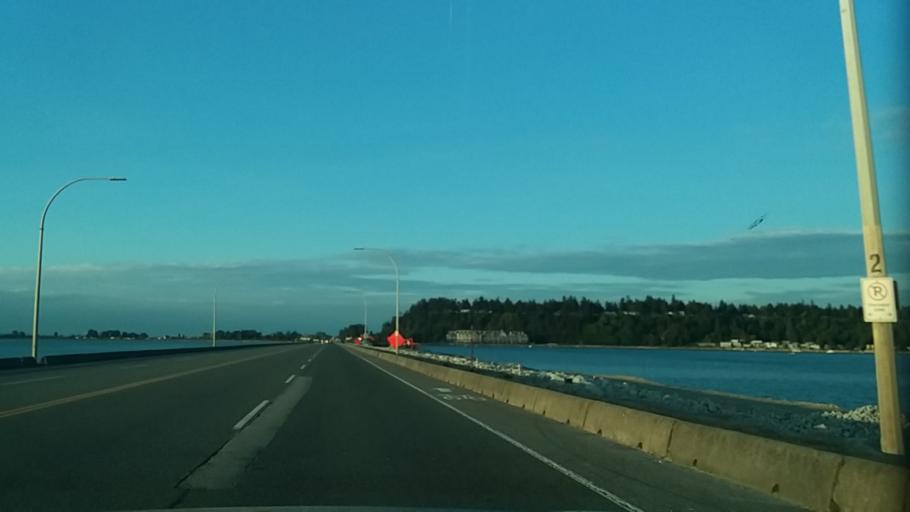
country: US
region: Washington
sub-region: Whatcom County
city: Point Roberts
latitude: 49.0167
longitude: -123.1155
